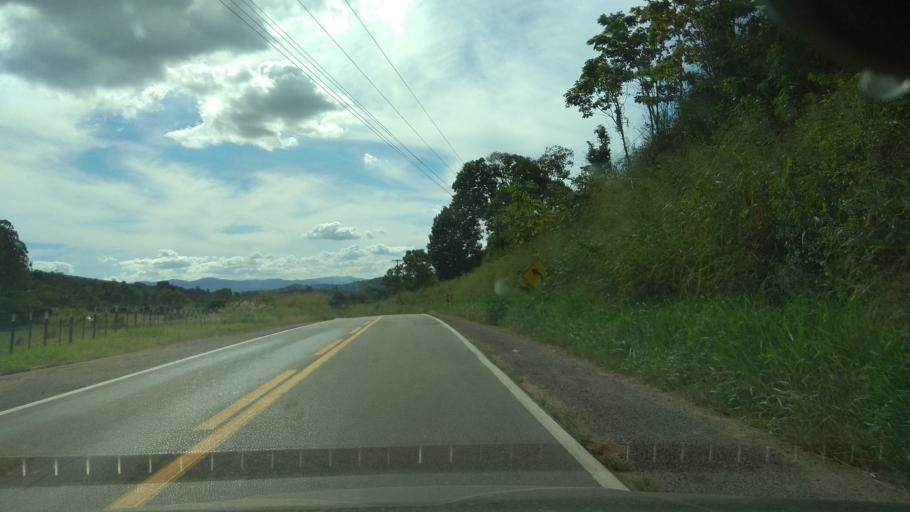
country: BR
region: Bahia
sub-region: Ipiau
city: Ipiau
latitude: -14.0754
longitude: -39.7843
